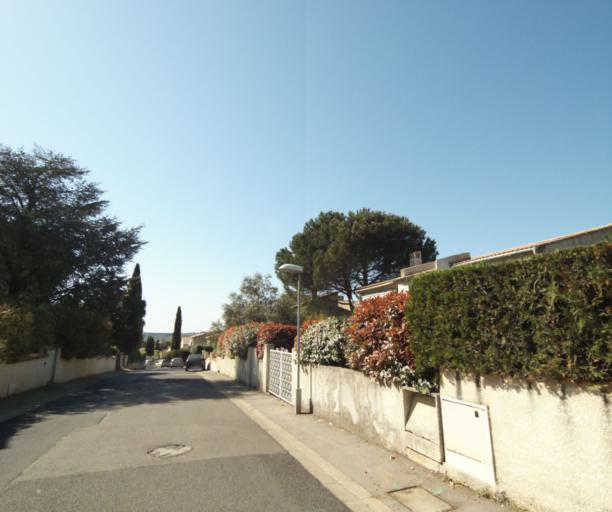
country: FR
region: Languedoc-Roussillon
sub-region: Departement de l'Herault
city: Le Cres
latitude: 43.6481
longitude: 3.9345
